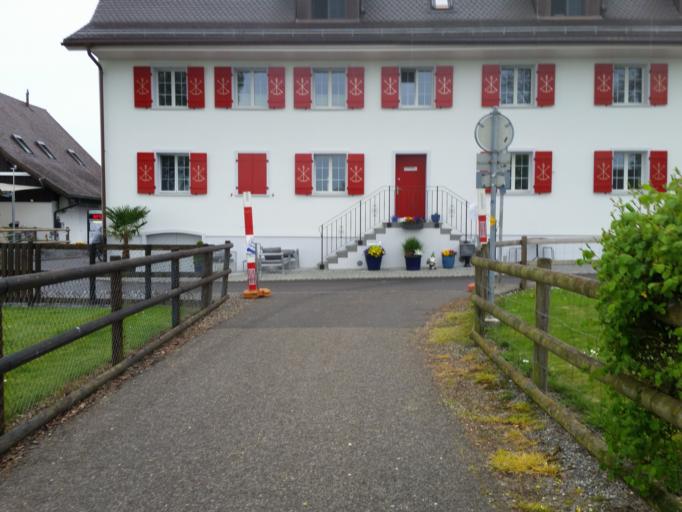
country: CH
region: Thurgau
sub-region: Arbon District
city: Uttwil
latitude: 47.5861
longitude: 9.3426
